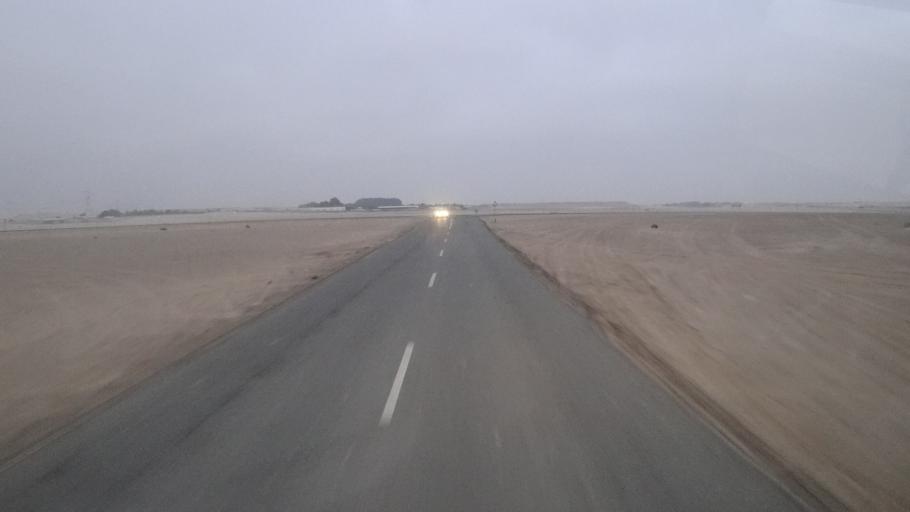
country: AE
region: Abu Dhabi
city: Abu Dhabi
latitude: 24.1753
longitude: 54.6974
